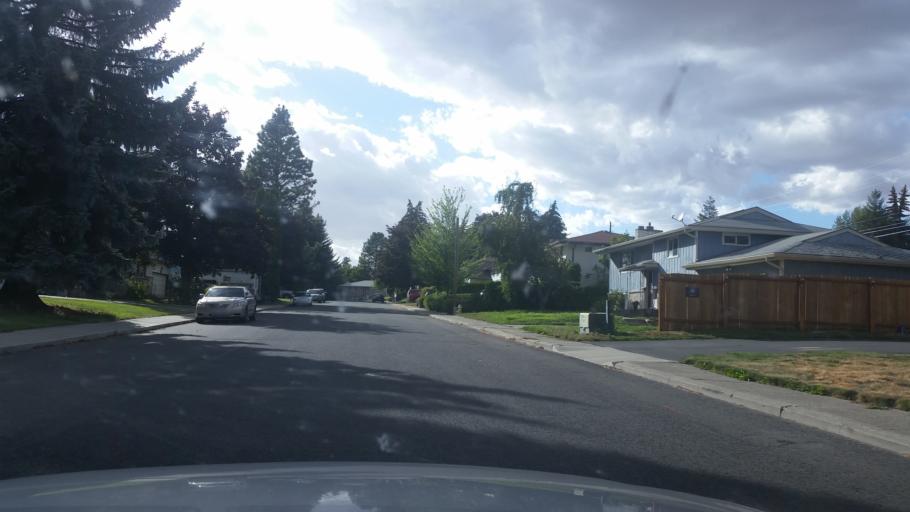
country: US
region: Washington
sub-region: Spokane County
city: Cheney
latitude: 47.4815
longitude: -117.5982
